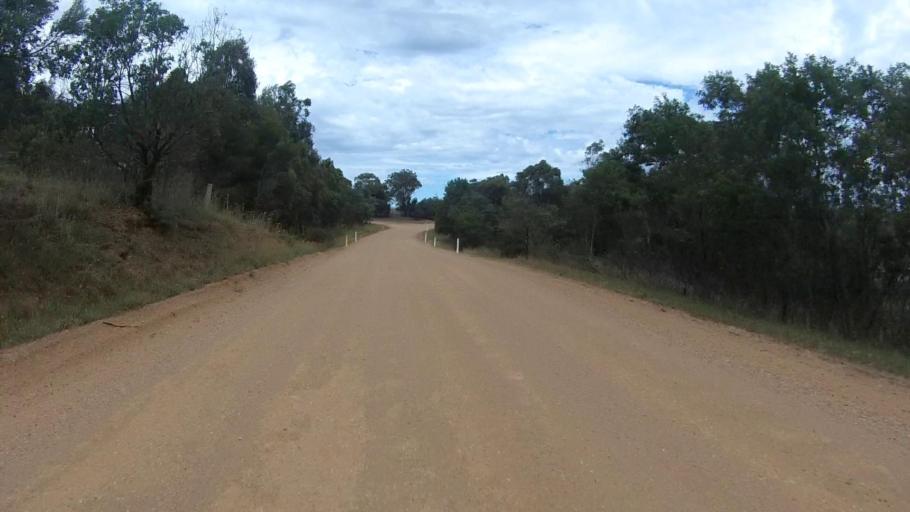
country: AU
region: Tasmania
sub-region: Sorell
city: Sorell
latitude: -42.6966
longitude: 147.4629
